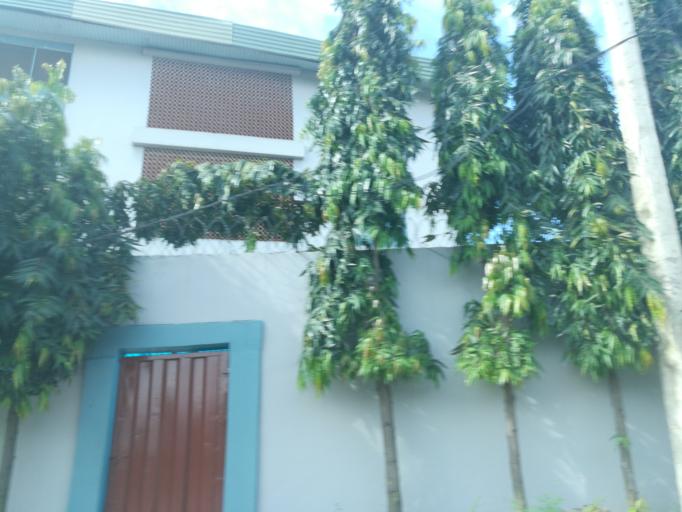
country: NG
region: Lagos
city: Agege
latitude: 6.6246
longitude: 3.3507
